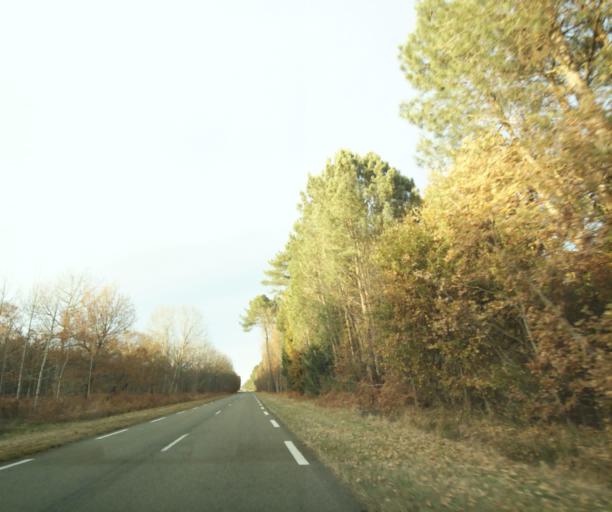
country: FR
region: Aquitaine
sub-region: Departement de la Gironde
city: Grignols
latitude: 44.1927
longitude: -0.1542
